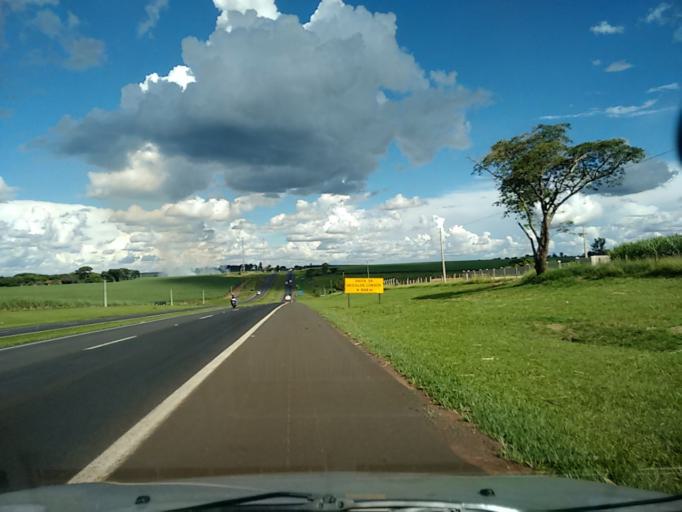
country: BR
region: Sao Paulo
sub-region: Ibate
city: Ibate
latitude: -21.9083
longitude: -48.0517
